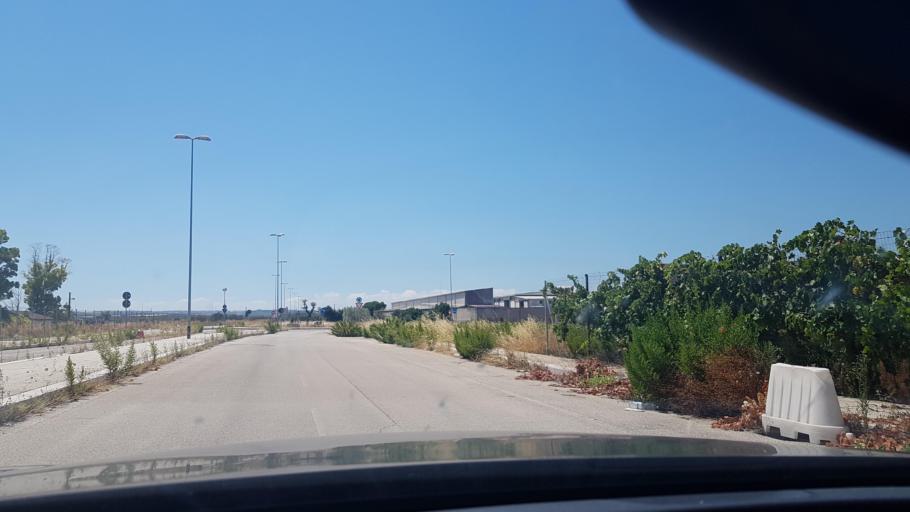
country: IT
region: Apulia
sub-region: Provincia di Barletta - Andria - Trani
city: Barletta
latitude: 41.3043
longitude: 16.3307
